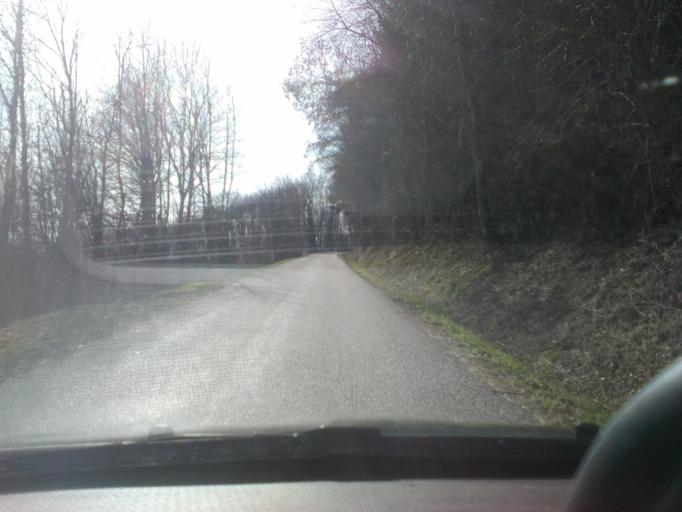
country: FR
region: Lorraine
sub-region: Departement des Vosges
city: Ban-de-Laveline
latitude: 48.3455
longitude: 7.0939
